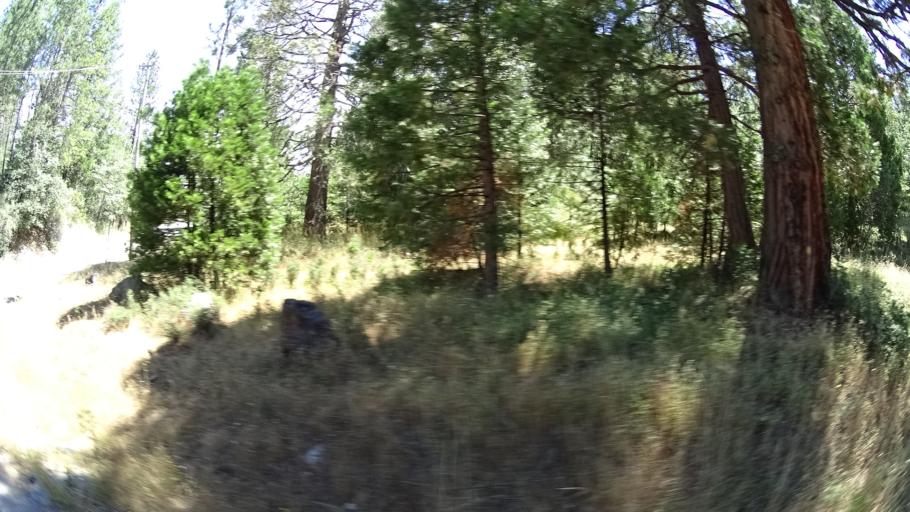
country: US
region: California
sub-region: Amador County
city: Pioneer
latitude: 38.3498
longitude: -120.5181
